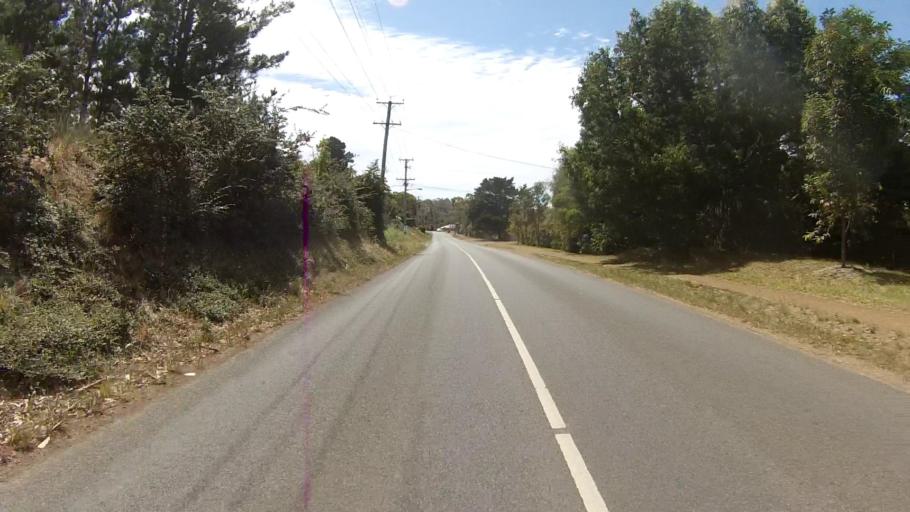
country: AU
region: Tasmania
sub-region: Kingborough
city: Blackmans Bay
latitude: -43.0271
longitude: 147.4167
